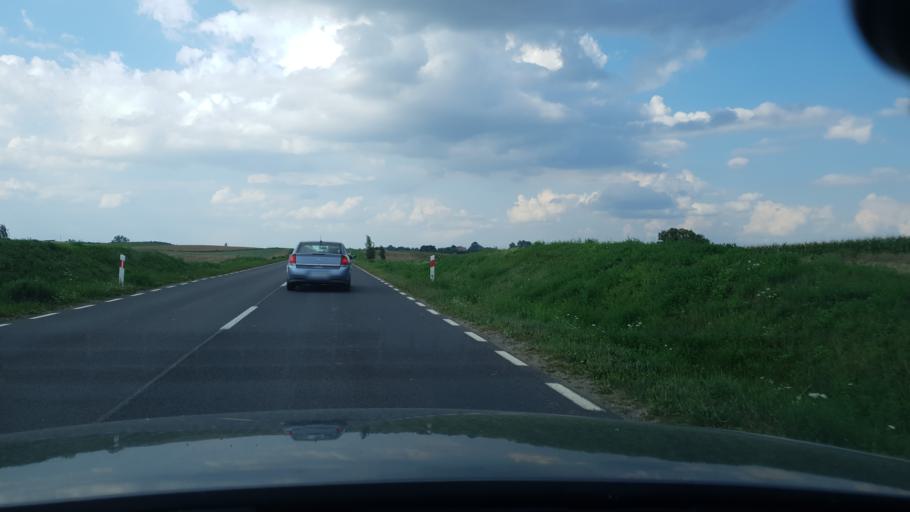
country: PL
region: Kujawsko-Pomorskie
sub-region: Powiat wabrzeski
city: Wabrzezno
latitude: 53.2965
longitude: 18.9261
